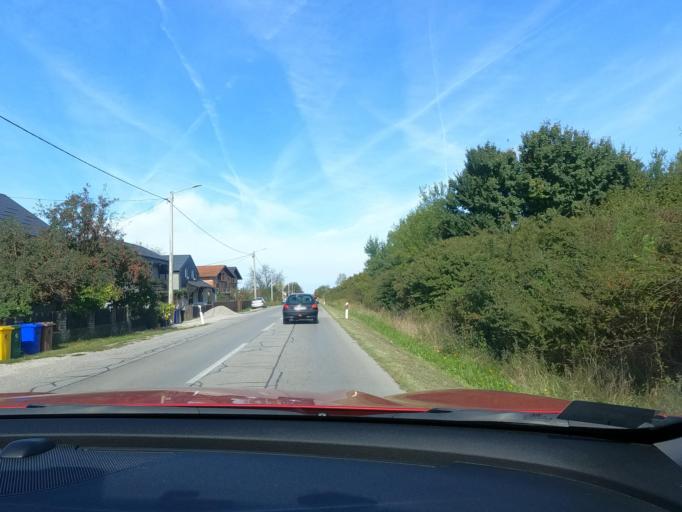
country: HR
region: Sisacko-Moslavacka
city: Petrinja
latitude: 45.4168
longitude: 16.2919
